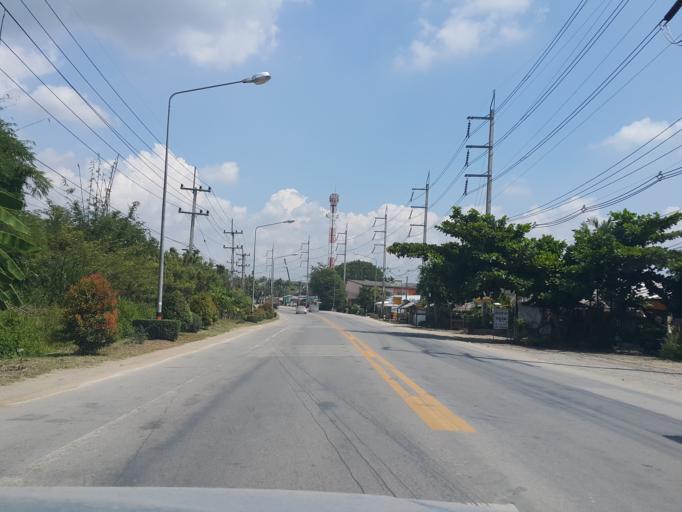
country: TH
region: Chiang Mai
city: San Sai
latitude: 18.9195
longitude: 98.9888
